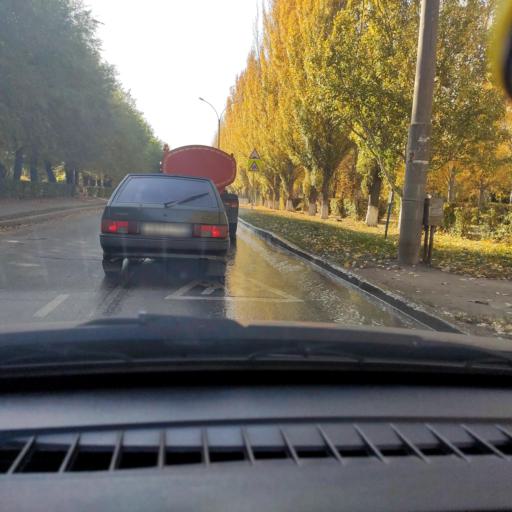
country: RU
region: Samara
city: Tol'yatti
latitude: 53.5316
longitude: 49.2925
